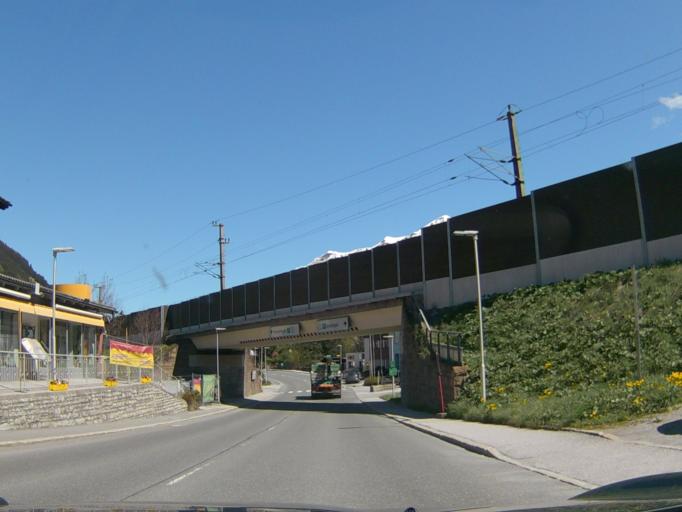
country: AT
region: Salzburg
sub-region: Politischer Bezirk Sankt Johann im Pongau
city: Bad Gastein
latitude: 47.1070
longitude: 13.1347
